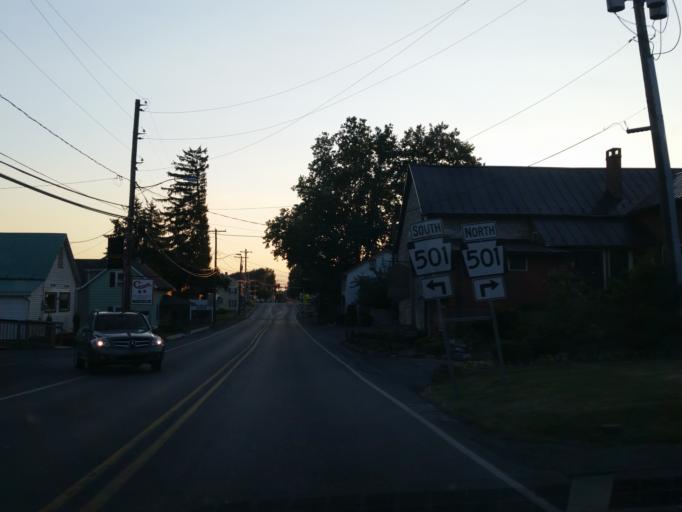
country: US
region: Pennsylvania
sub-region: Lancaster County
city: Brickerville
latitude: 40.2985
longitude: -76.3022
